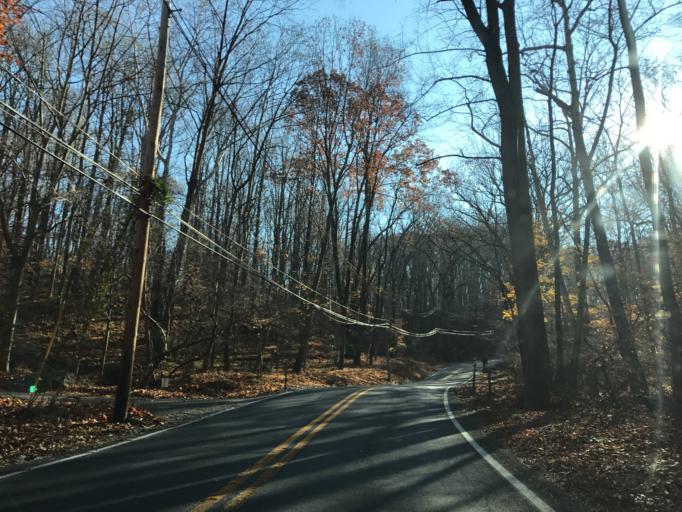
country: US
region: Maryland
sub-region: Howard County
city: Ellicott City
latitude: 39.2596
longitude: -76.7975
